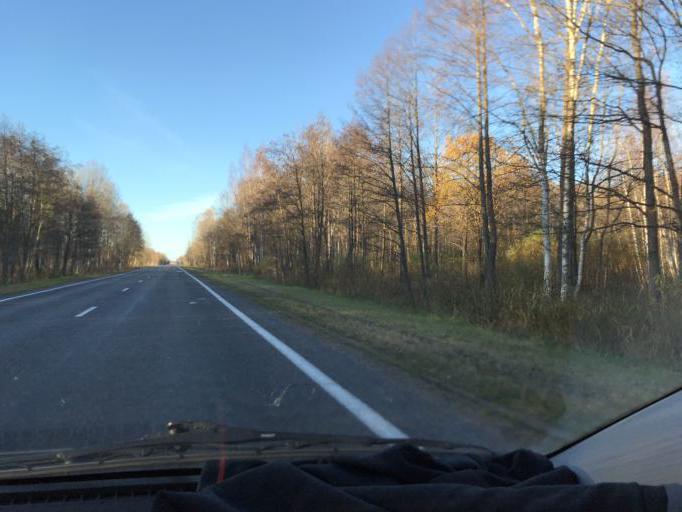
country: BY
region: Vitebsk
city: Haradok
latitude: 55.3773
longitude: 30.1457
